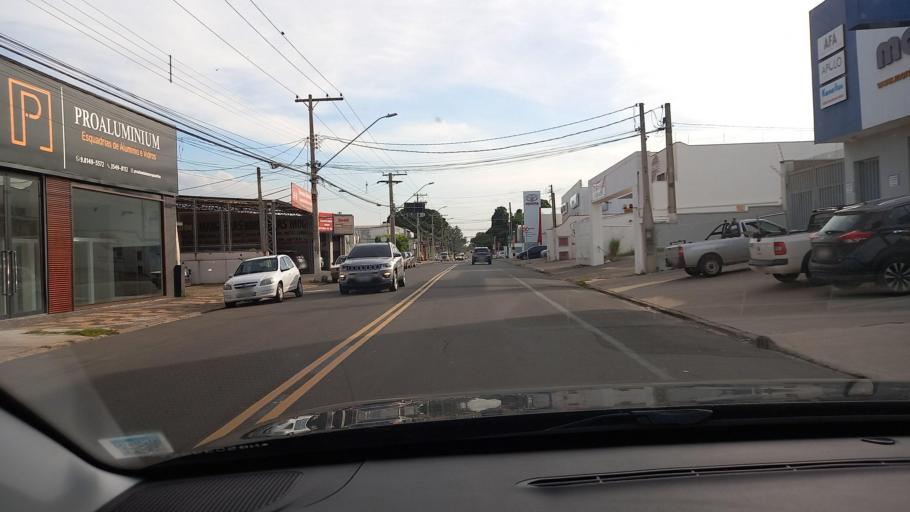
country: BR
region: Sao Paulo
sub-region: Mogi-Mirim
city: Mogi Mirim
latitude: -22.4431
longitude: -46.9709
